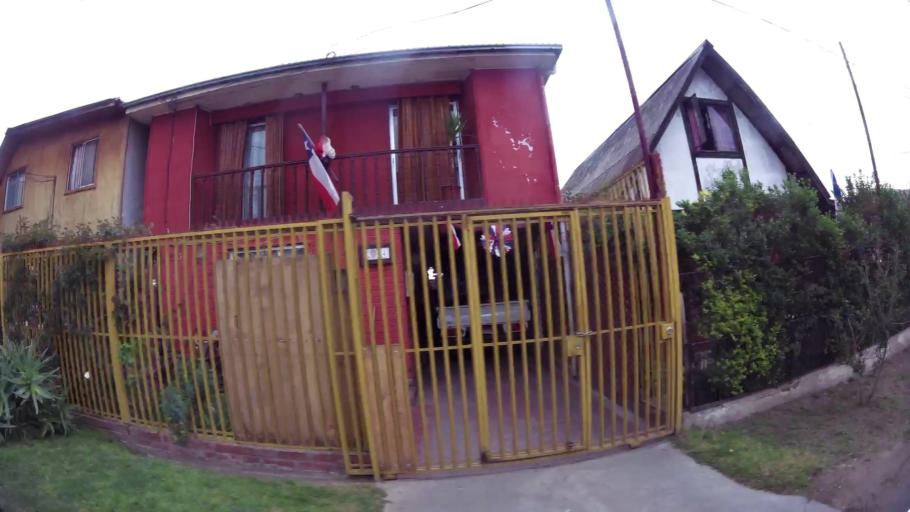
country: CL
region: Santiago Metropolitan
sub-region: Provincia de Santiago
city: Lo Prado
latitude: -33.5013
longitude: -70.7748
